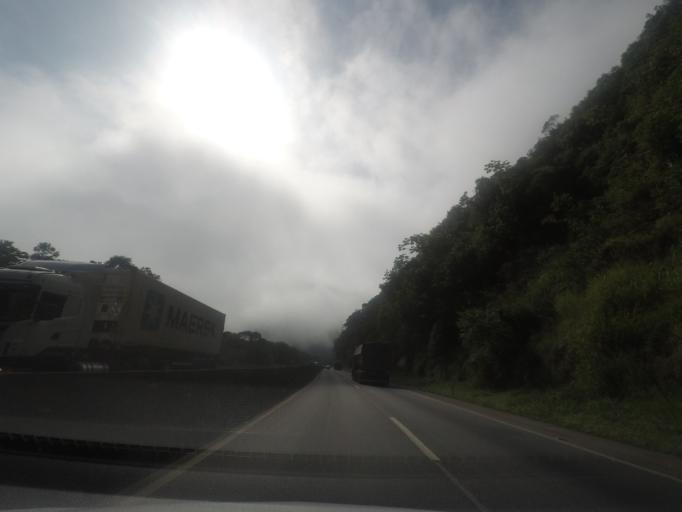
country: BR
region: Parana
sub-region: Antonina
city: Antonina
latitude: -25.5937
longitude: -48.8837
